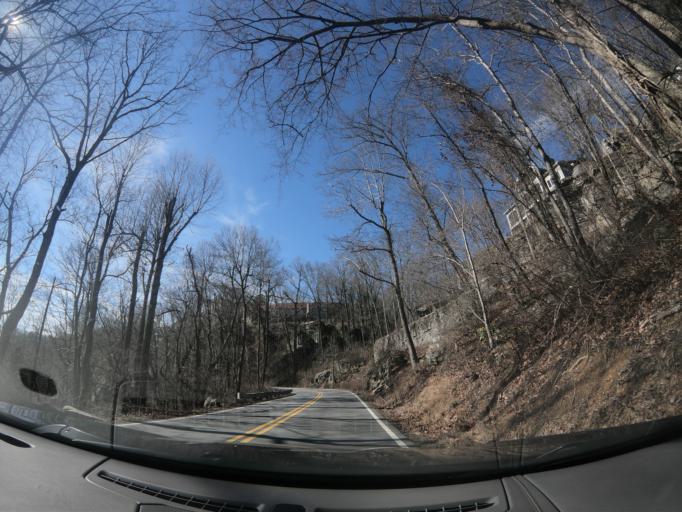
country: US
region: Georgia
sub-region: Walker County
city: Lookout Mountain
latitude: 34.9799
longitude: -85.3468
